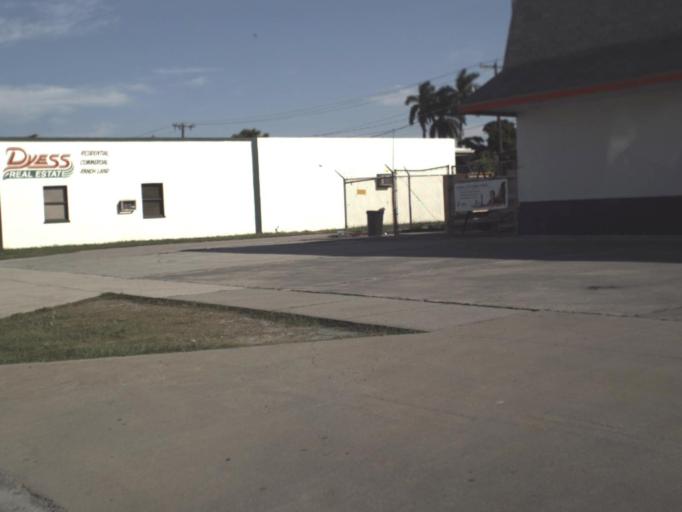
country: US
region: Florida
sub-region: Hendry County
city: Clewiston
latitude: 26.7542
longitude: -80.9297
